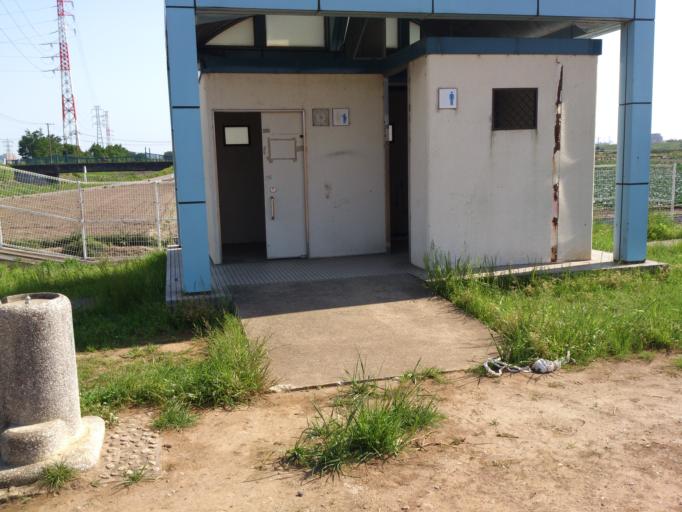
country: JP
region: Chiba
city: Matsudo
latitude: 35.7659
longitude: 139.8908
